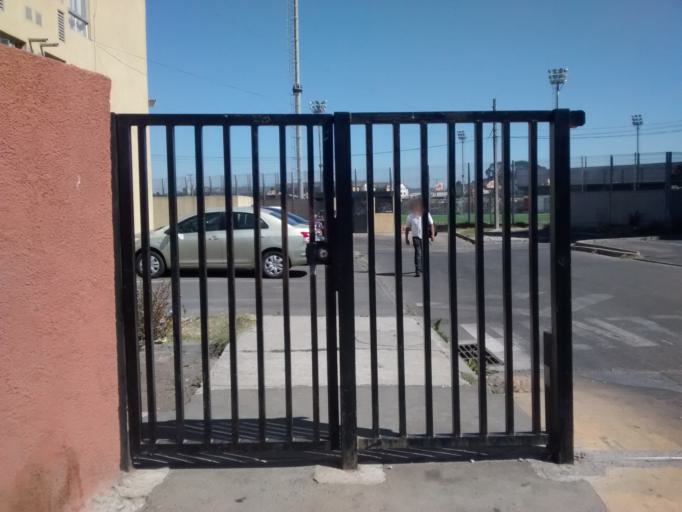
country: CL
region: Biobio
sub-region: Provincia de Concepcion
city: Concepcion
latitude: -36.8106
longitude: -73.0611
